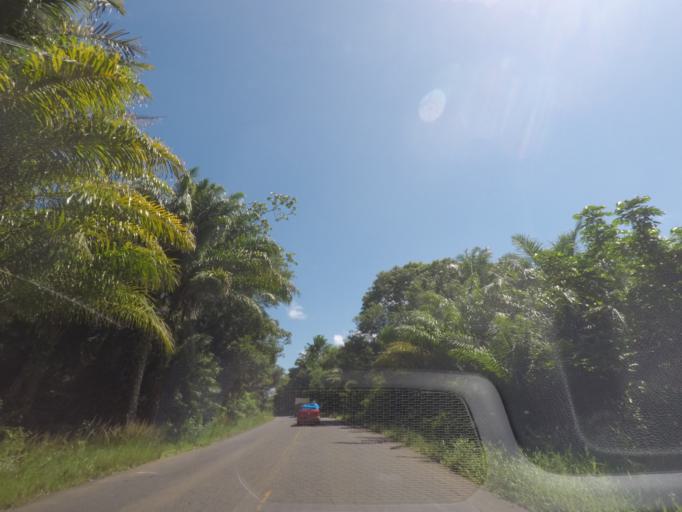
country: BR
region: Bahia
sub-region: Taperoa
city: Taperoa
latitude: -13.4608
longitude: -39.0893
